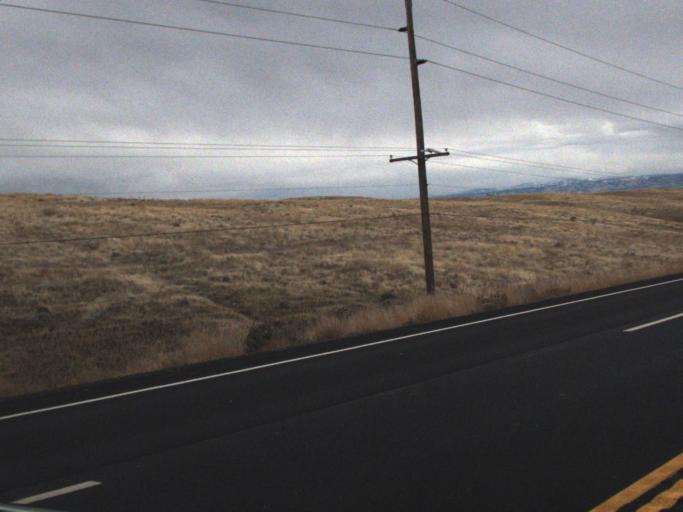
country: US
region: Washington
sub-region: Walla Walla County
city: Garrett
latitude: 46.0552
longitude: -118.7181
